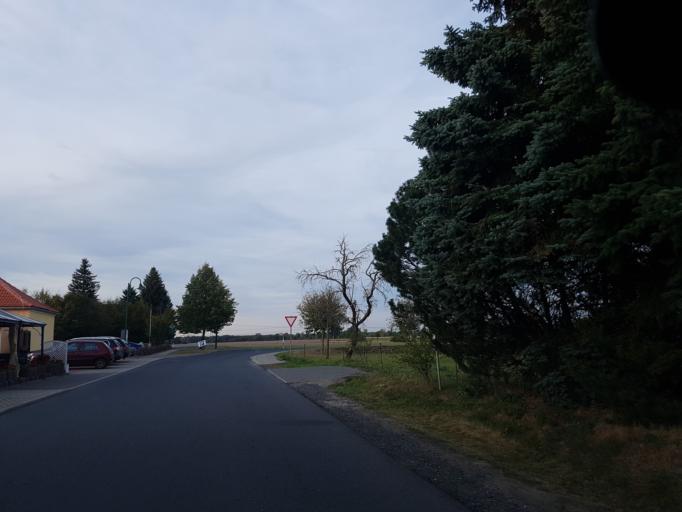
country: DE
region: Saxony
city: Wulknitz
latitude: 51.3606
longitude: 13.4066
